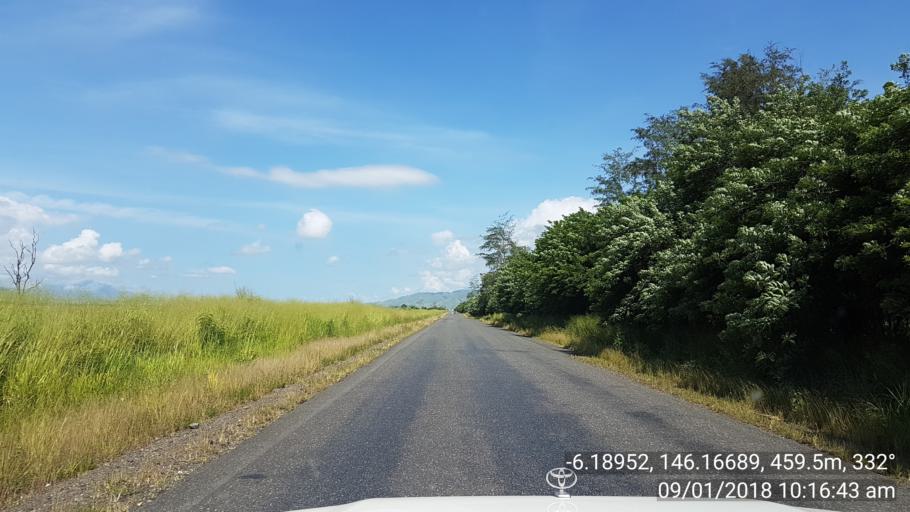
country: PG
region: Eastern Highlands
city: Kainantu
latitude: -6.1899
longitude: 146.1671
